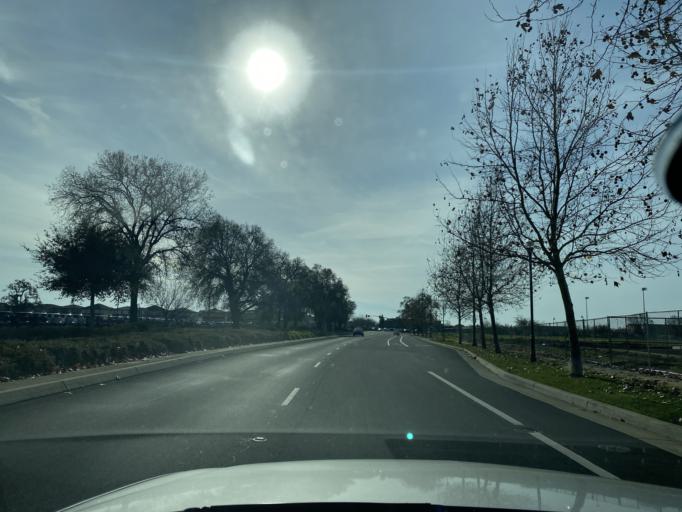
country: US
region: California
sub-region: Sacramento County
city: Elk Grove
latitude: 38.4035
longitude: -121.3949
